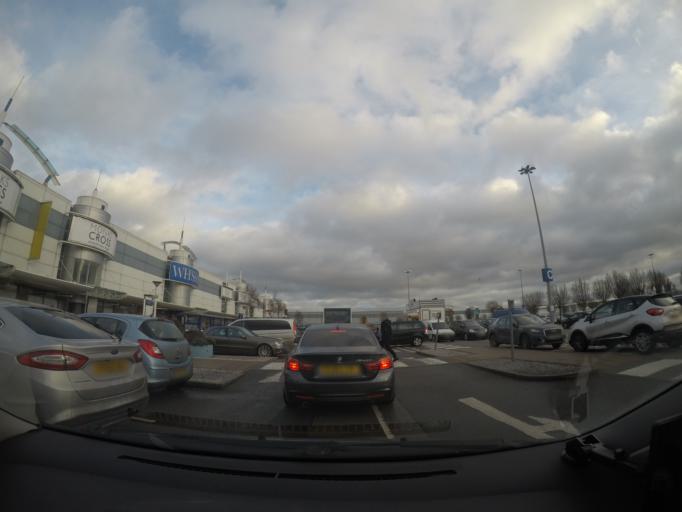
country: GB
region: England
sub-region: City of York
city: Huntington
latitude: 53.9882
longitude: -1.0457
